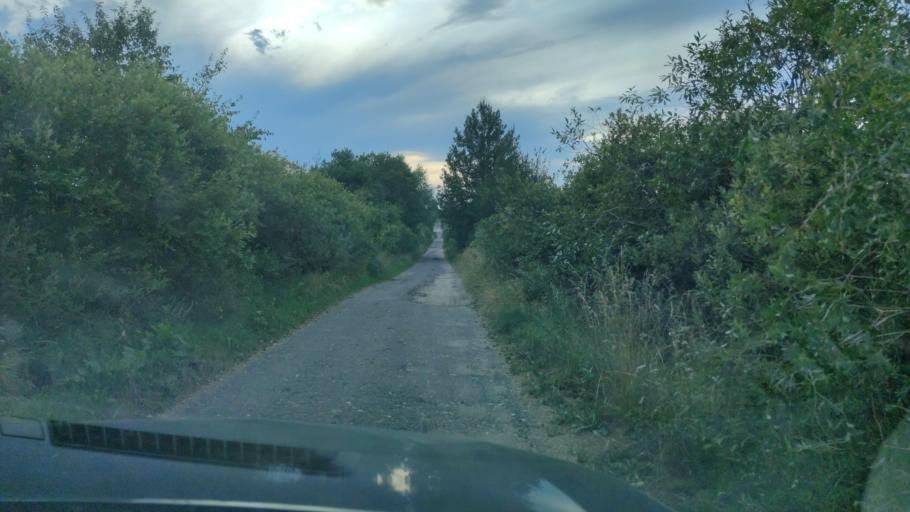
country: BY
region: Vitebsk
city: Mosar
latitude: 55.1273
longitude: 27.1641
